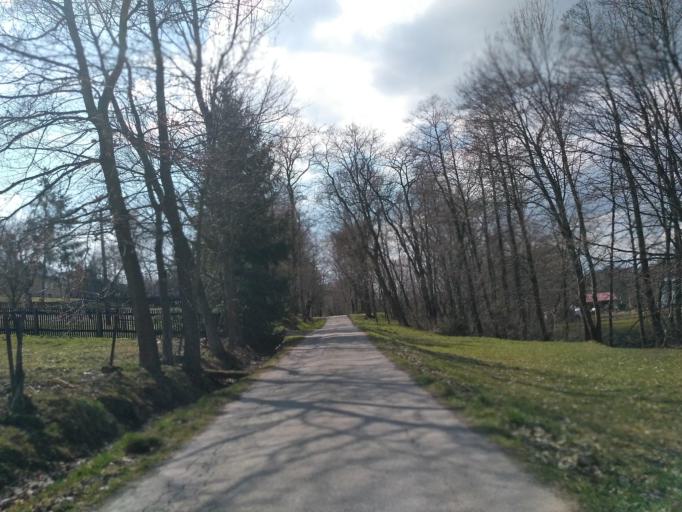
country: PL
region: Subcarpathian Voivodeship
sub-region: Powiat ropczycko-sedziszowski
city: Iwierzyce
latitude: 49.9953
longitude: 21.7445
